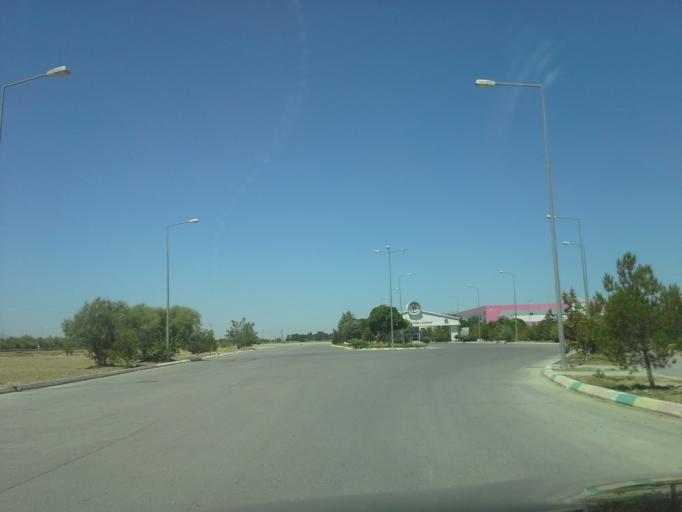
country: TM
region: Ahal
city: Ashgabat
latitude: 38.0020
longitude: 58.3010
